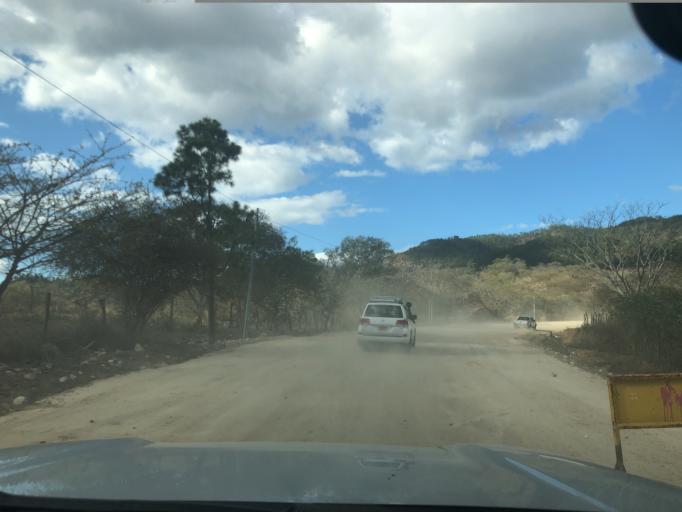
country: NI
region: Nueva Segovia
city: Ocotal
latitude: 13.6639
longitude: -86.6136
